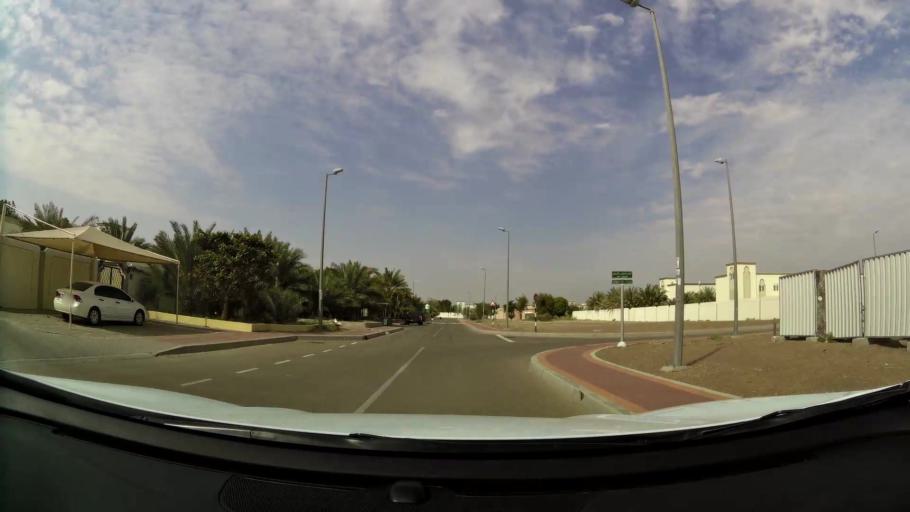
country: AE
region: Abu Dhabi
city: Al Ain
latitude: 24.0987
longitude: 55.8908
